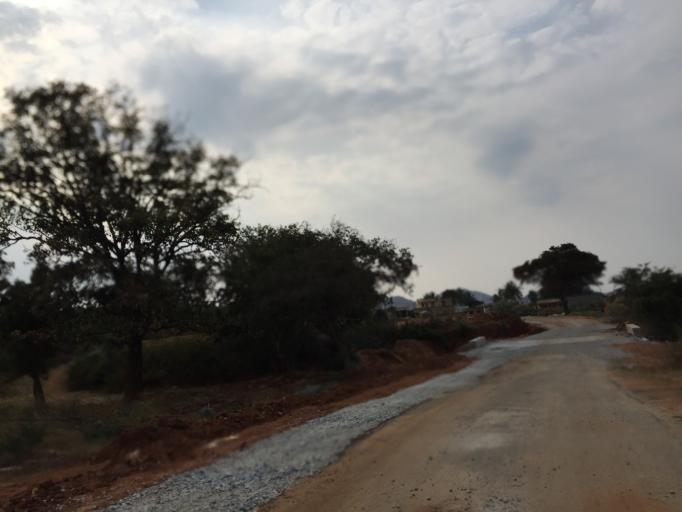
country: IN
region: Karnataka
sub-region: Chikkaballapur
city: Gudibanda
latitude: 13.5669
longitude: 77.7331
